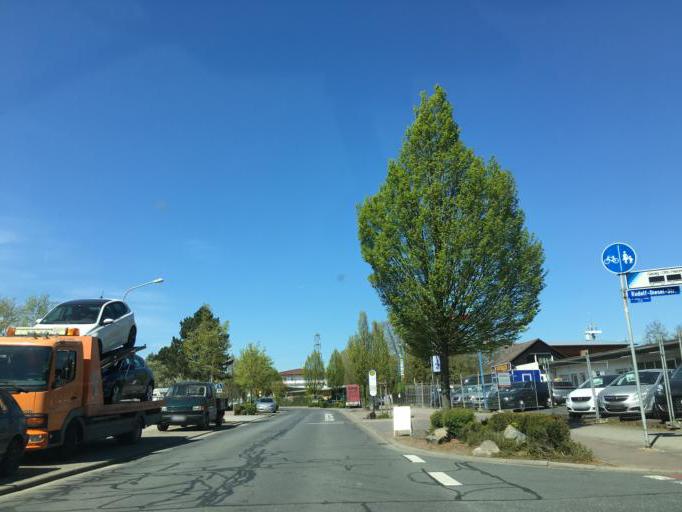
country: DE
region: Hesse
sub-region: Regierungsbezirk Darmstadt
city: Gross-Zimmern
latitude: 49.8811
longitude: 8.8182
